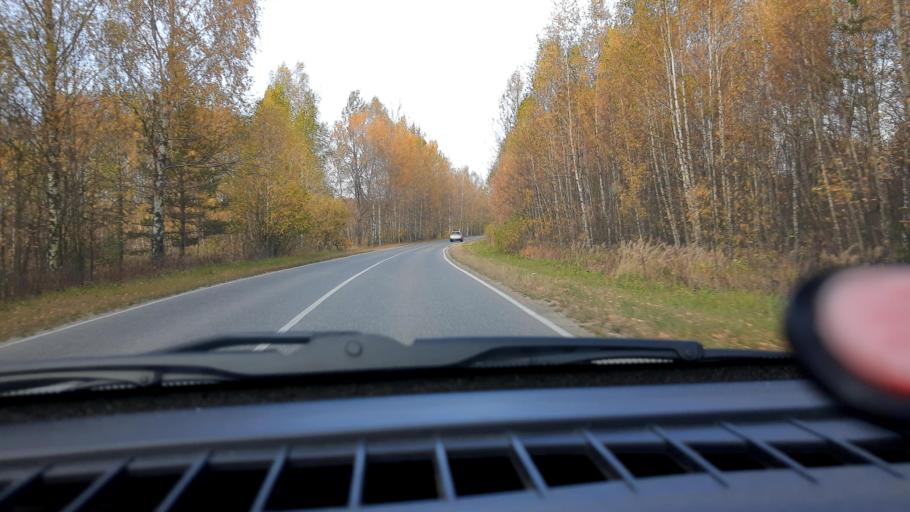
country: RU
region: Nizjnij Novgorod
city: Neklyudovo
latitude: 56.5052
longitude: 43.8444
